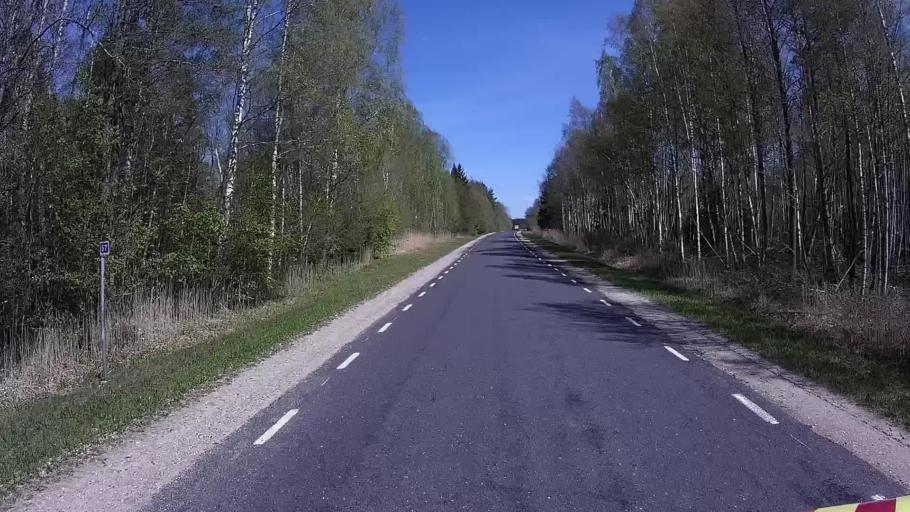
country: EE
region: Laeaene
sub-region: Ridala Parish
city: Uuemoisa
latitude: 59.0243
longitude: 23.8060
